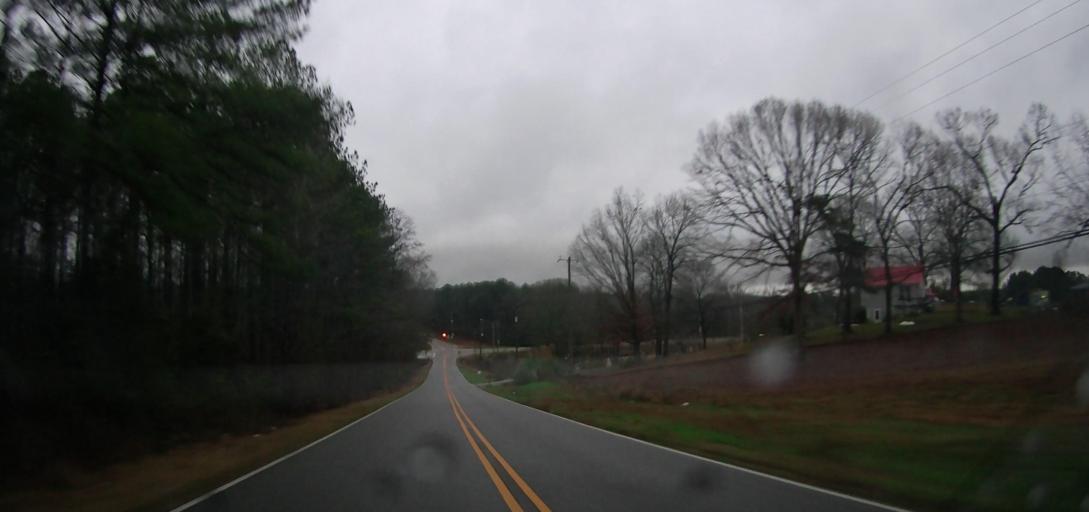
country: US
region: Alabama
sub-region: Bibb County
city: West Blocton
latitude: 33.1123
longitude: -87.1408
